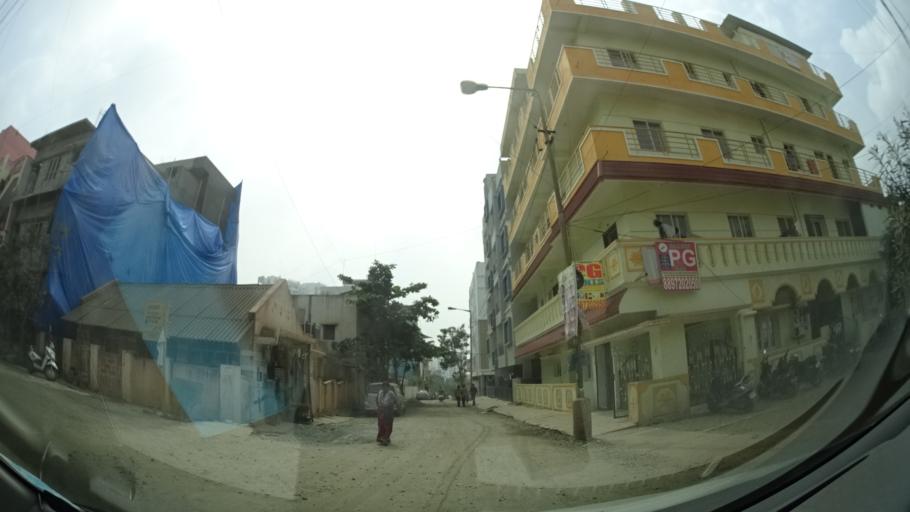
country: IN
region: Karnataka
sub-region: Bangalore Rural
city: Hoskote
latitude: 12.9791
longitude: 77.7534
